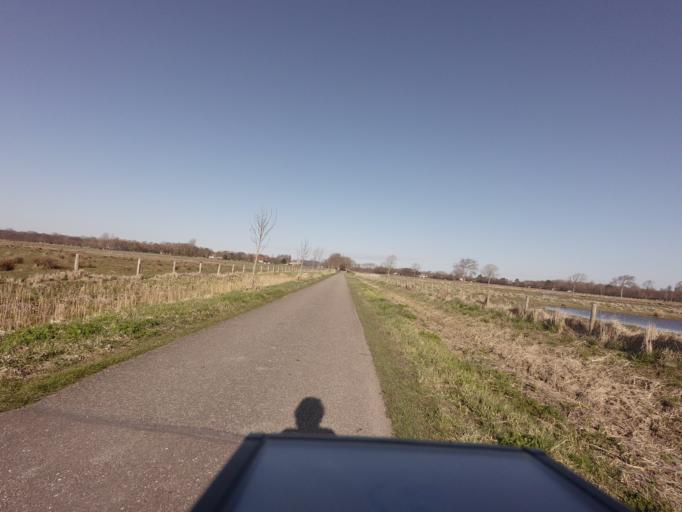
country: NL
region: Zeeland
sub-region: Schouwen-Duiveland
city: Haamstede
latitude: 51.7078
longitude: 3.7540
